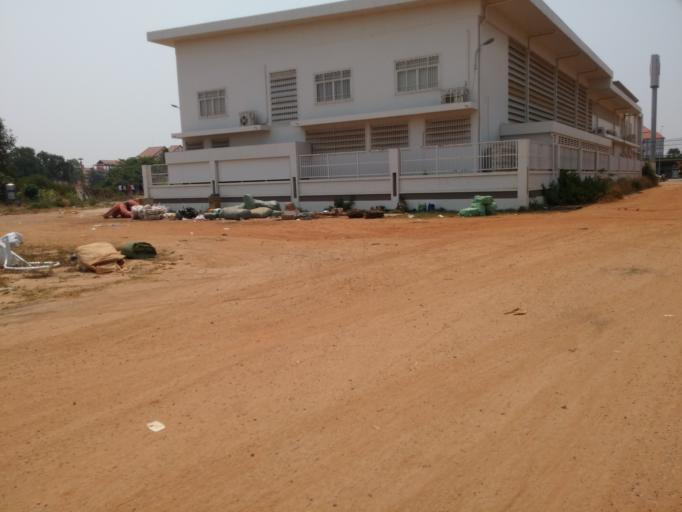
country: KH
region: Siem Reap
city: Siem Reap
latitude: 13.3592
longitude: 103.8909
